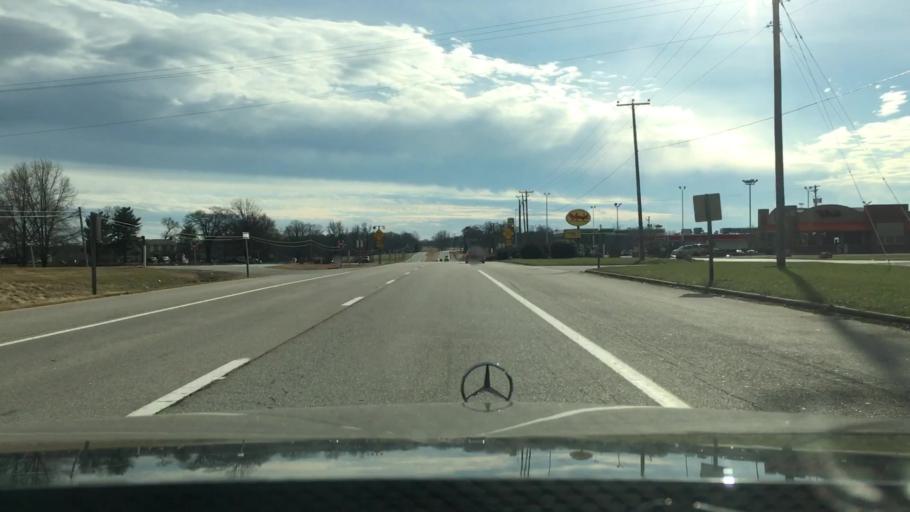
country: US
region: Virginia
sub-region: Pittsylvania County
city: Mount Hermon
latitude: 36.7348
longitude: -79.3816
